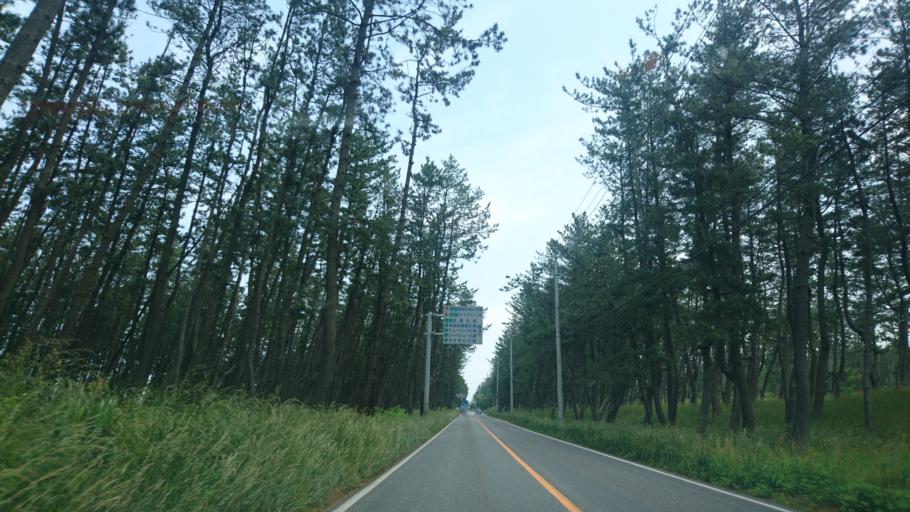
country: JP
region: Niigata
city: Shibata
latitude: 38.0311
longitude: 139.2924
